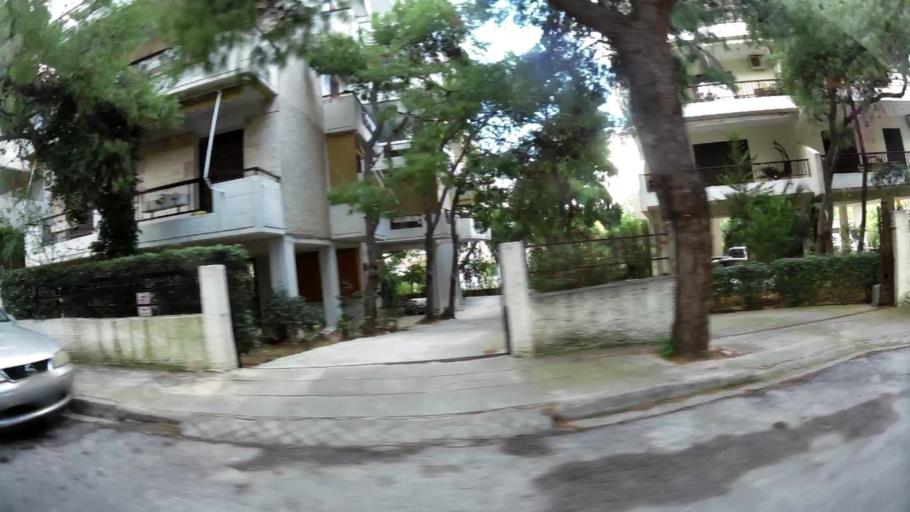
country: GR
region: Attica
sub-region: Nomarchia Athinas
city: Melissia
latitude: 38.0550
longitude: 23.8260
